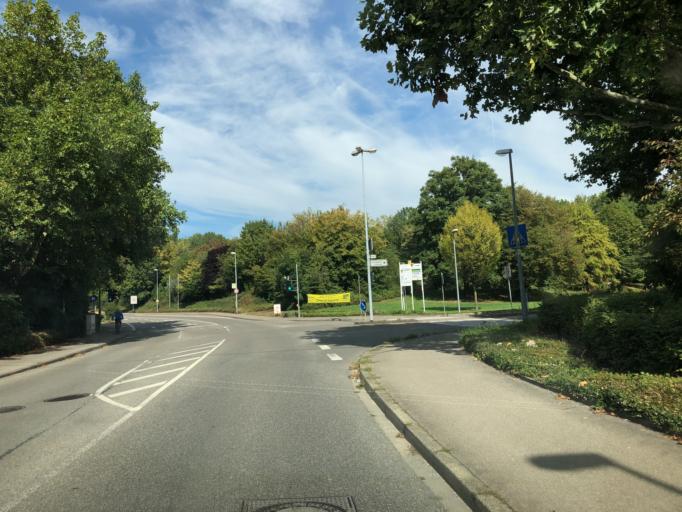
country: DE
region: Baden-Wuerttemberg
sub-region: Regierungsbezirk Stuttgart
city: Unterensingen
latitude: 48.6397
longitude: 9.3515
